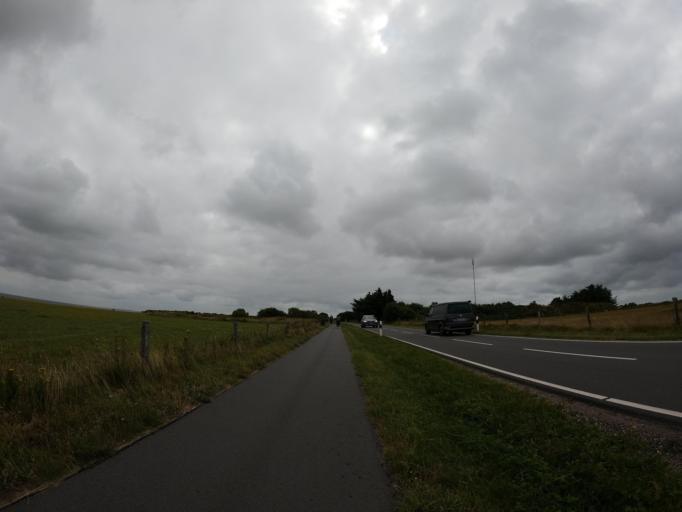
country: DE
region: Schleswig-Holstein
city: Tinnum
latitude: 54.9456
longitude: 8.3474
